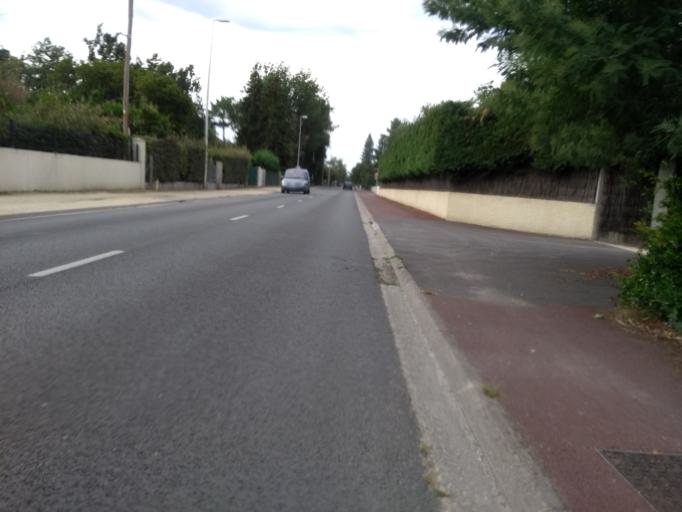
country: FR
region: Aquitaine
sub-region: Departement de la Gironde
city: Saint-Aubin-de-Medoc
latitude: 44.7759
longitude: -0.6949
